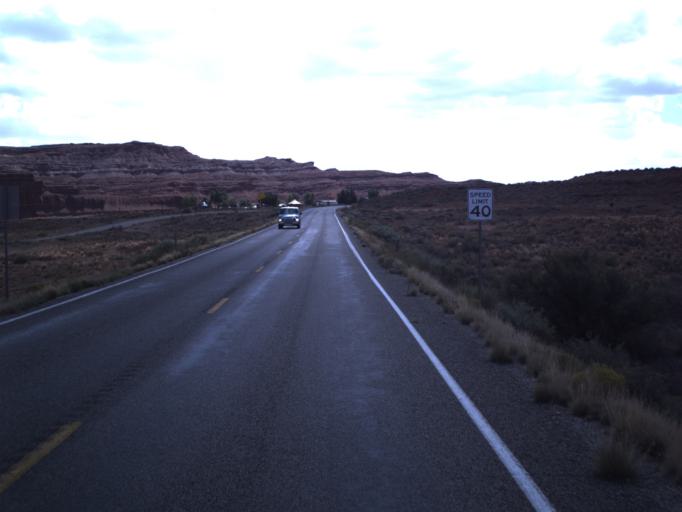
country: US
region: Arizona
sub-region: Navajo County
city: Kayenta
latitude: 37.1547
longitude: -109.8570
